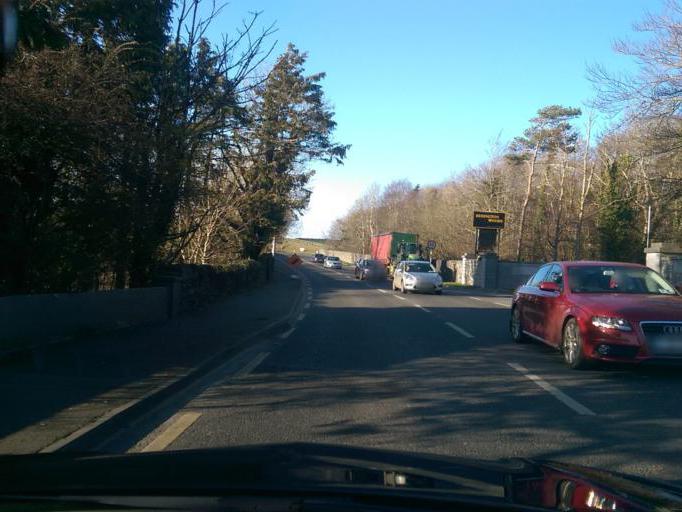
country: IE
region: Connaught
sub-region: County Galway
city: Oranmore
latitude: 53.2314
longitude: -8.8805
